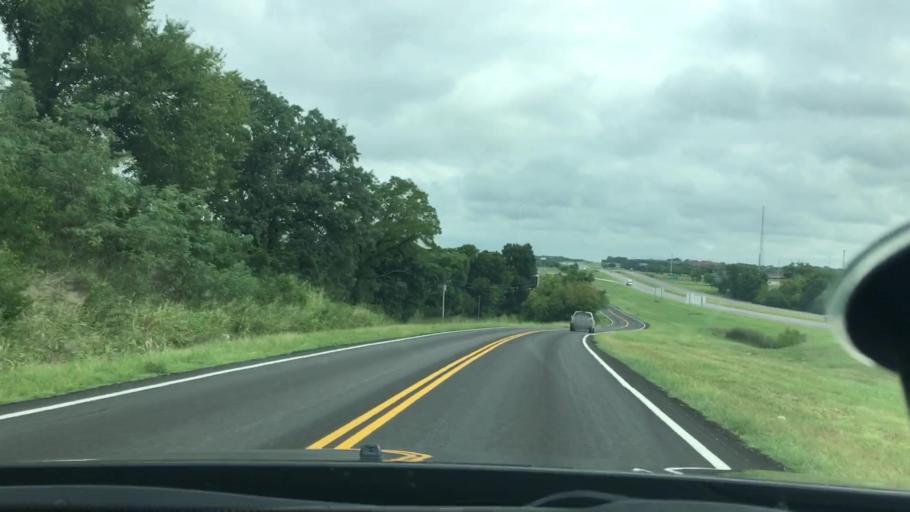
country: US
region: Oklahoma
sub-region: Bryan County
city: Durant
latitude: 34.0130
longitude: -96.3954
